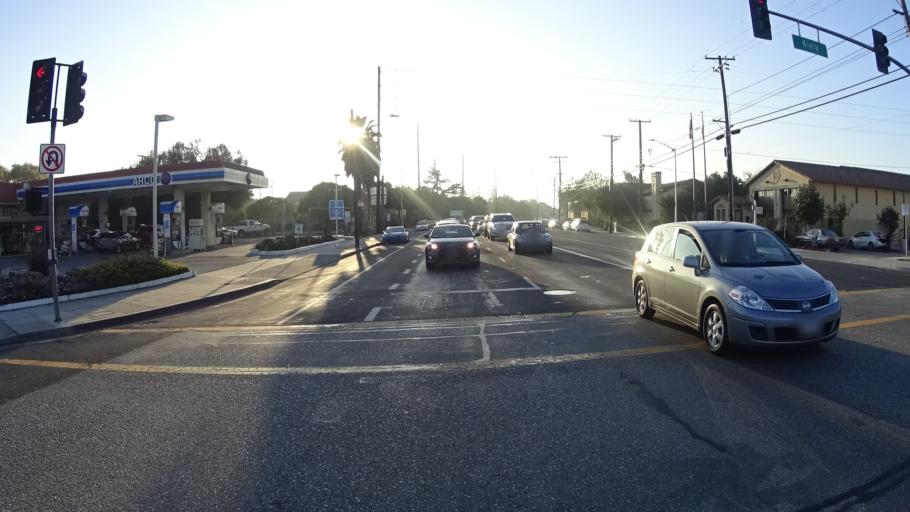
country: US
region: California
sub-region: Santa Clara County
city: Santa Clara
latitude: 37.3383
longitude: -121.9769
